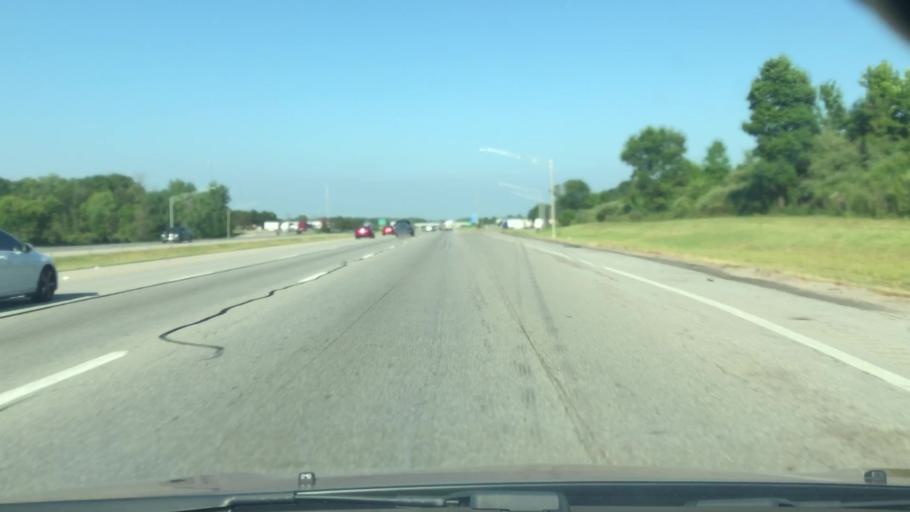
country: US
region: Ohio
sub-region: Madison County
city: Choctaw Lake
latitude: 39.9401
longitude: -83.5378
